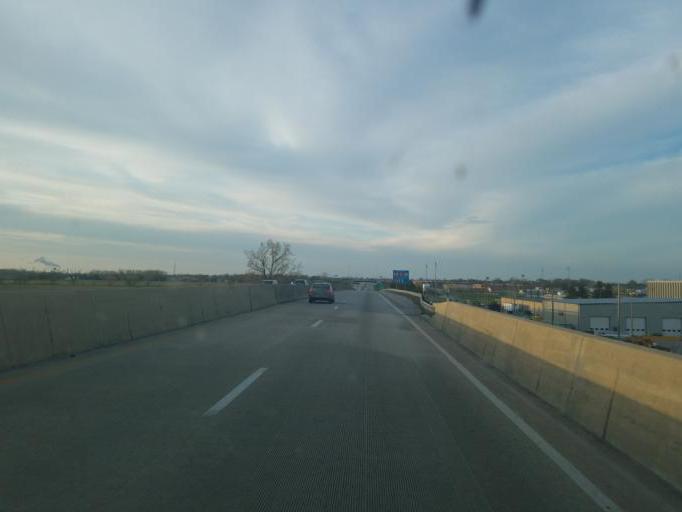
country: US
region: Ohio
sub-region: Wood County
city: Northwood
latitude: 41.5988
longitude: -83.4769
